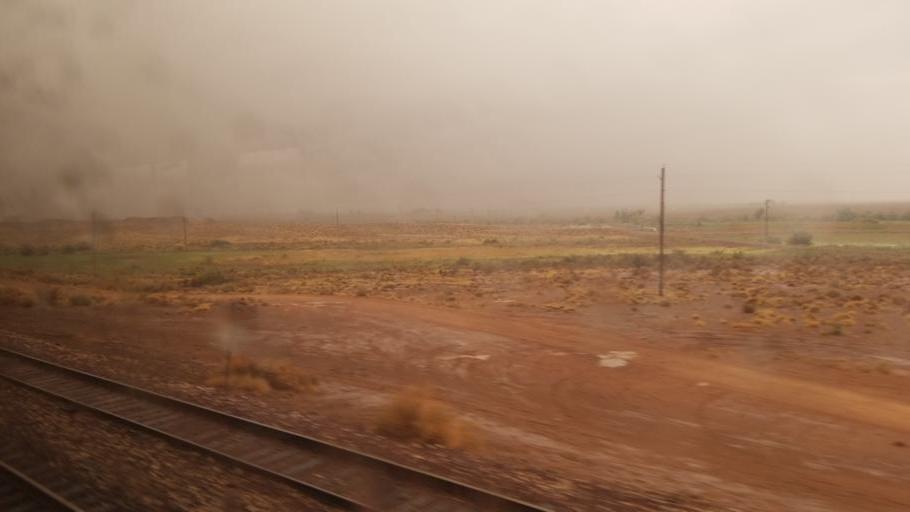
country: US
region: Arizona
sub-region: Navajo County
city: Joseph City
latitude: 34.9084
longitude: -110.2604
